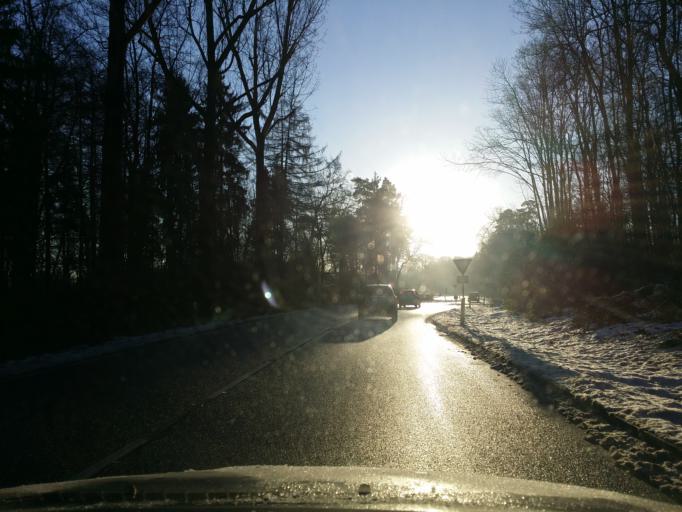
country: DE
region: Hesse
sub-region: Regierungsbezirk Darmstadt
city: Niedernhausen
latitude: 50.1435
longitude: 8.3288
